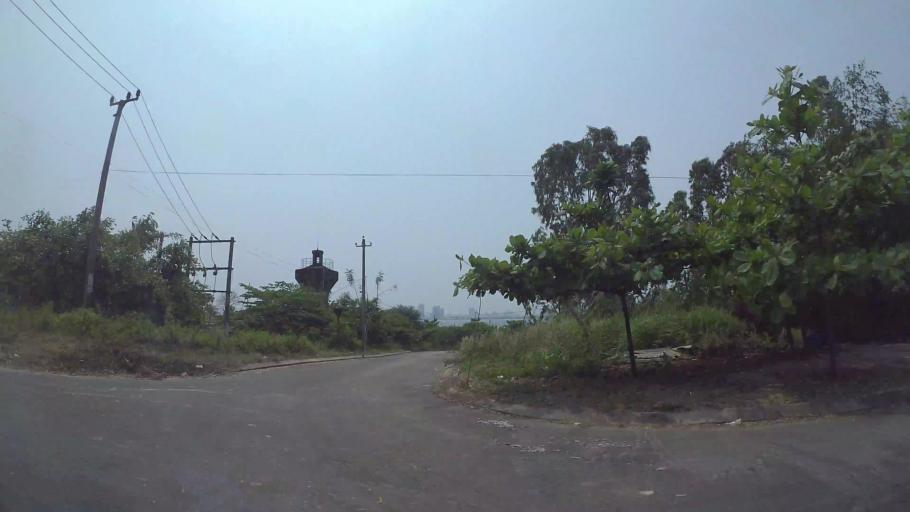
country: VN
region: Da Nang
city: Son Tra
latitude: 16.0978
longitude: 108.2673
